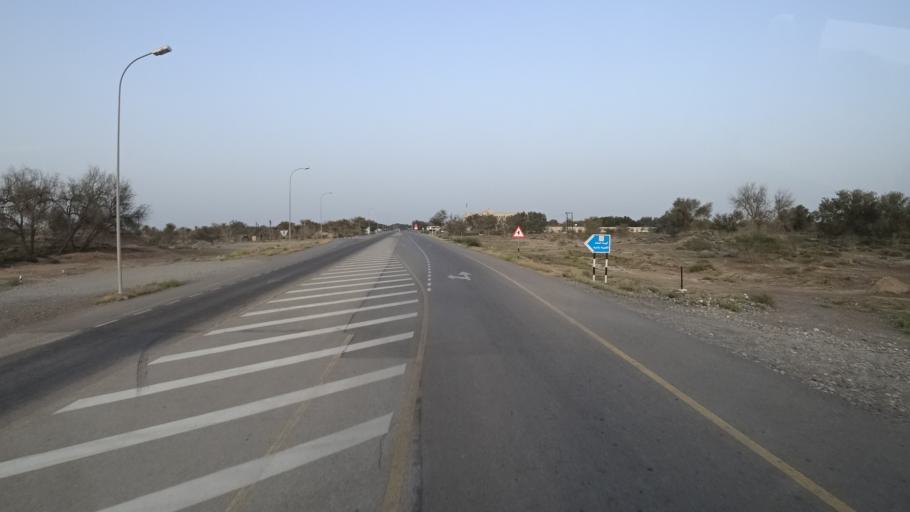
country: OM
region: Muhafazat Masqat
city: Muscat
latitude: 23.2045
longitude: 58.9539
